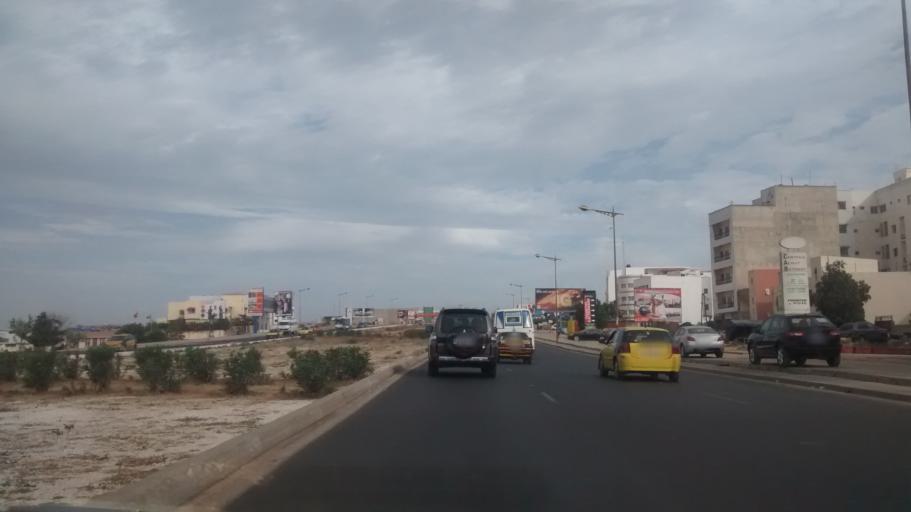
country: SN
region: Dakar
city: Mermoz Boabab
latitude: 14.7296
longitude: -17.4725
